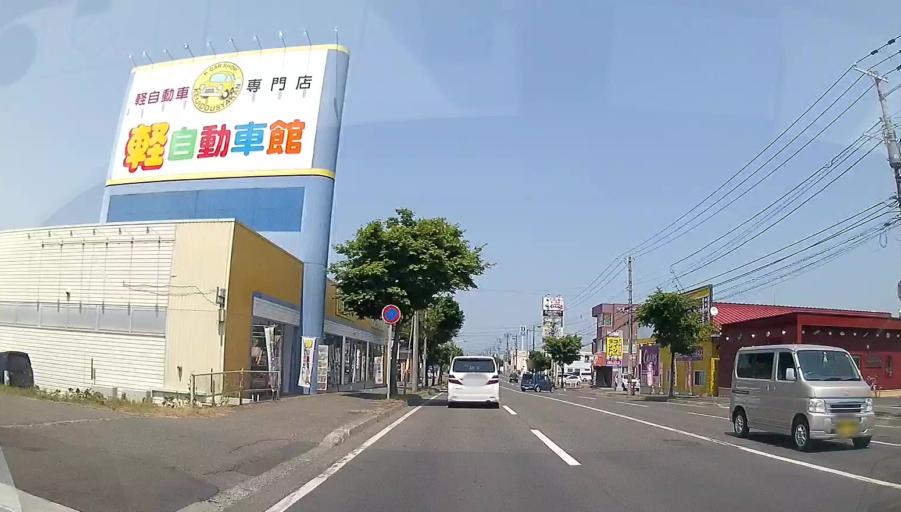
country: JP
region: Hokkaido
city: Obihiro
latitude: 42.8953
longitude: 143.2008
